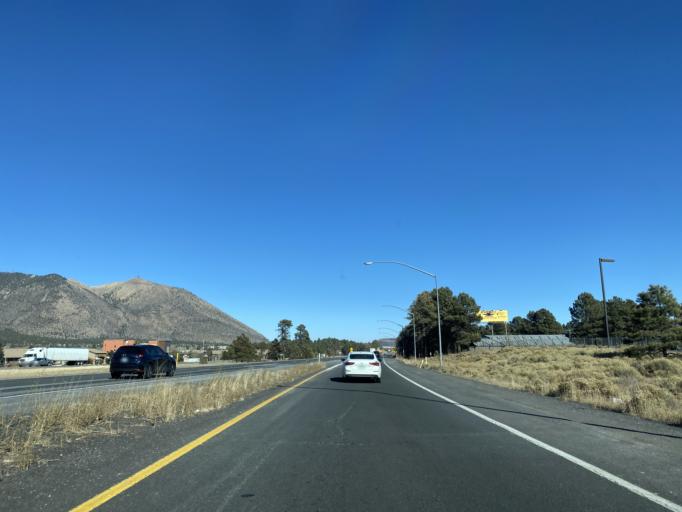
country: US
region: Arizona
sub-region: Coconino County
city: Flagstaff
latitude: 35.1933
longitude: -111.6188
